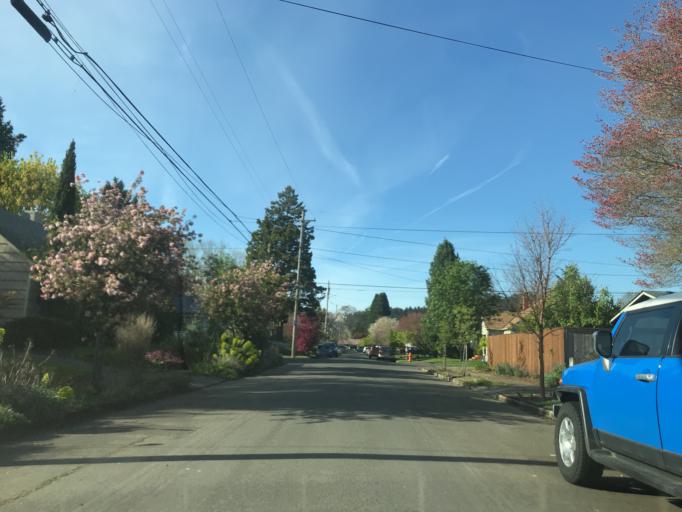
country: US
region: Oregon
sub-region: Multnomah County
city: Lents
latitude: 45.4985
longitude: -122.5986
